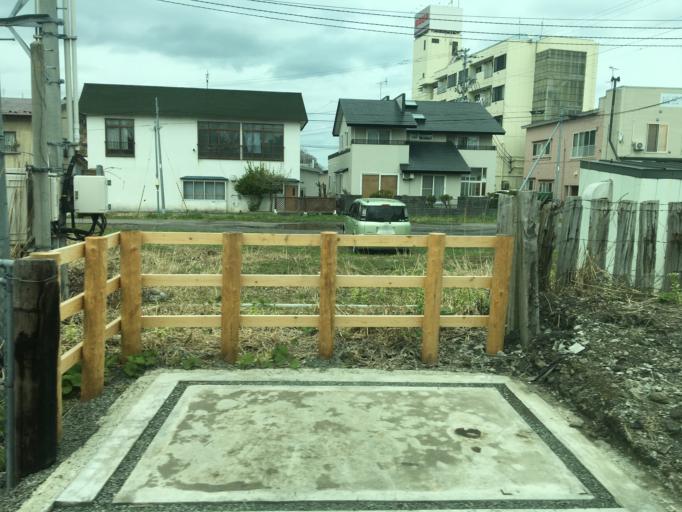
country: JP
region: Aomori
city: Shimokizukuri
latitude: 40.7751
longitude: 140.2203
